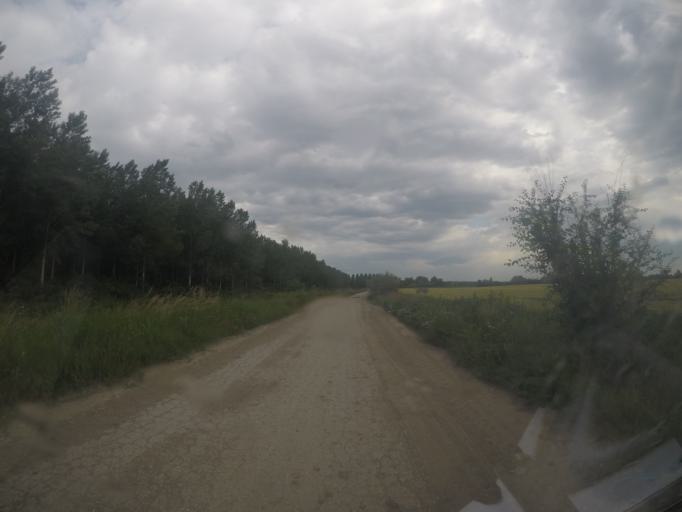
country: RS
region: Central Serbia
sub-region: Belgrade
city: Zemun
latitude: 44.8735
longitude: 20.3858
